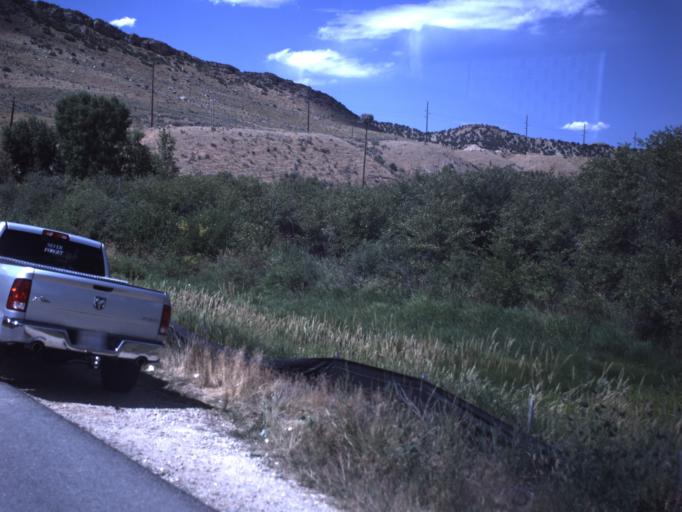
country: US
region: Utah
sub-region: Summit County
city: Coalville
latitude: 40.9120
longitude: -111.4069
